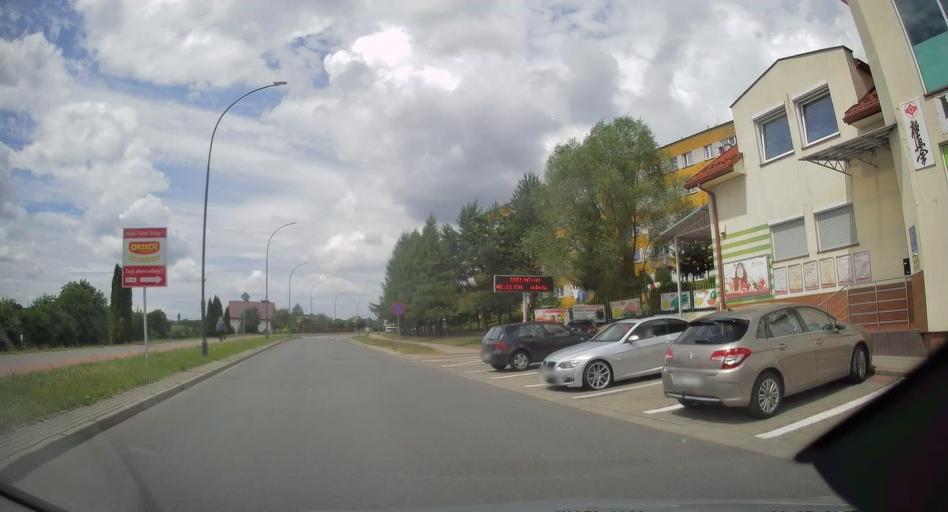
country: PL
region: Subcarpathian Voivodeship
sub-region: Powiat ropczycko-sedziszowski
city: Ropczyce
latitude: 50.0557
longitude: 21.6021
